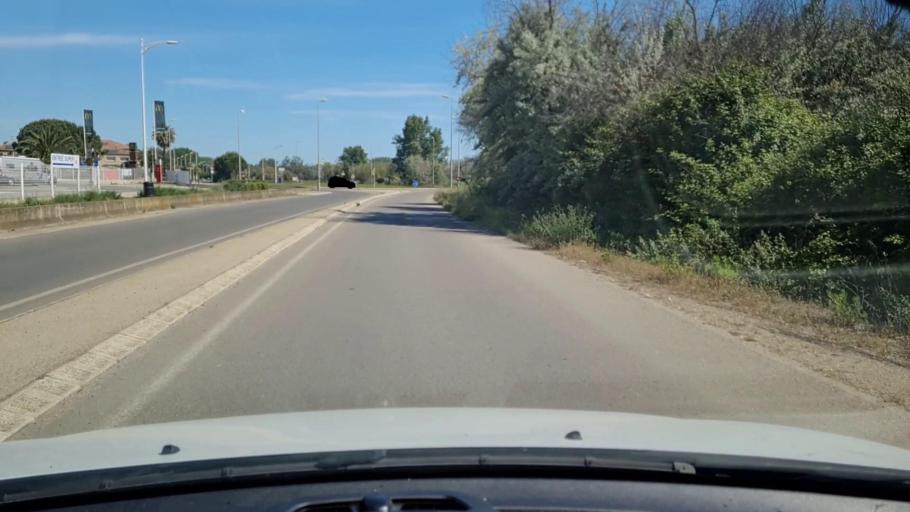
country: FR
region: Languedoc-Roussillon
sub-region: Departement du Gard
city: Le Grau-du-Roi
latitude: 43.5159
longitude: 4.1504
